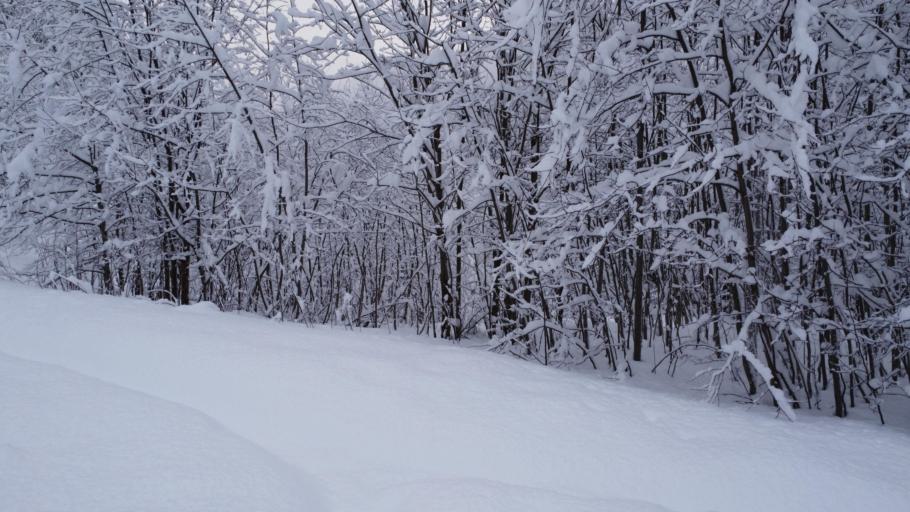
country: NO
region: Nordland
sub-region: Rana
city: Mo i Rana
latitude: 66.3321
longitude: 14.1648
